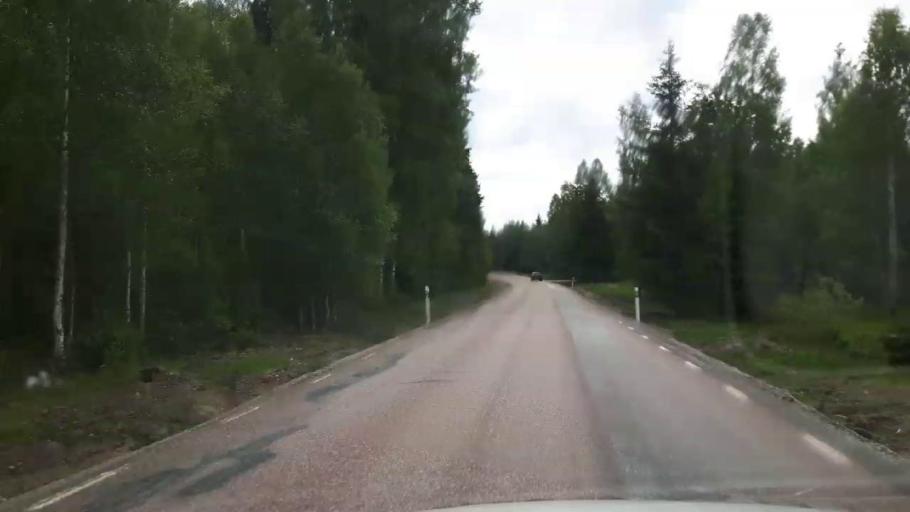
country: SE
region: Vaestmanland
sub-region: Skinnskattebergs Kommun
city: Skinnskatteberg
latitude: 59.8312
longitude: 15.8330
